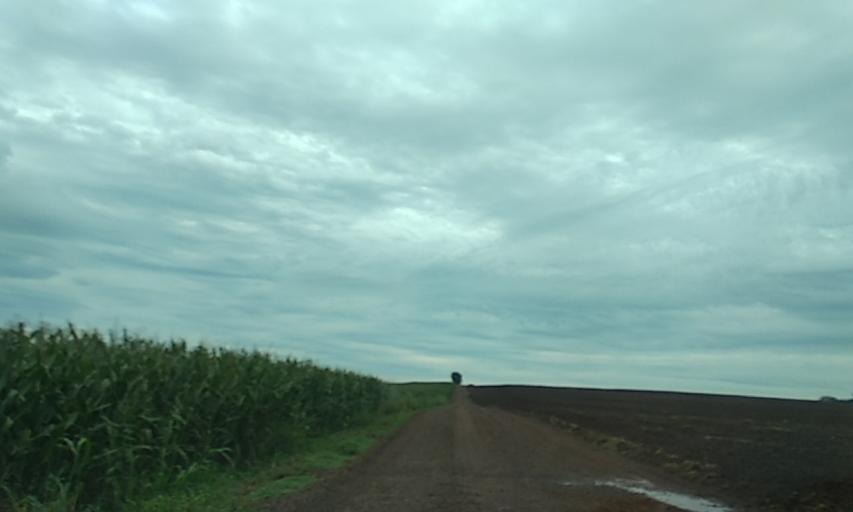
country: BR
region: Parana
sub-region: Marechal Candido Rondon
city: Marechal Candido Rondon
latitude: -24.5299
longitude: -54.0866
